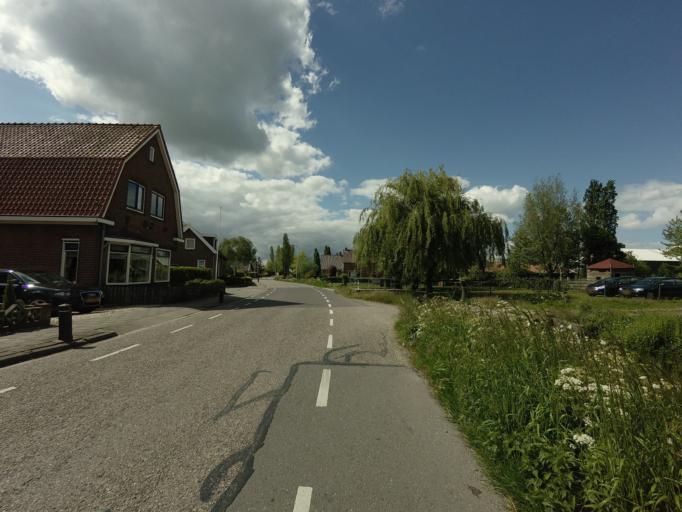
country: NL
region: South Holland
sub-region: Gemeente Leerdam
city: Leerdam
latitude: 51.9120
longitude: 5.0433
